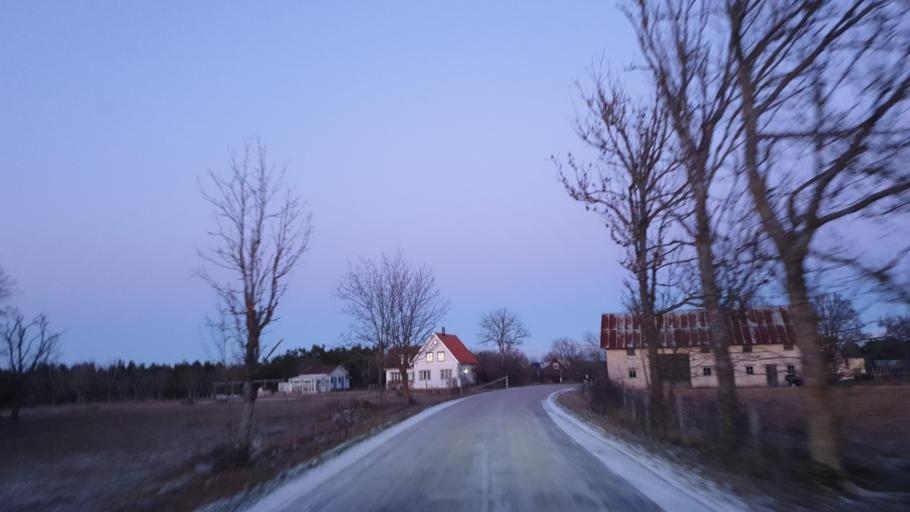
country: SE
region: Gotland
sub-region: Gotland
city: Slite
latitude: 57.4234
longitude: 18.8273
